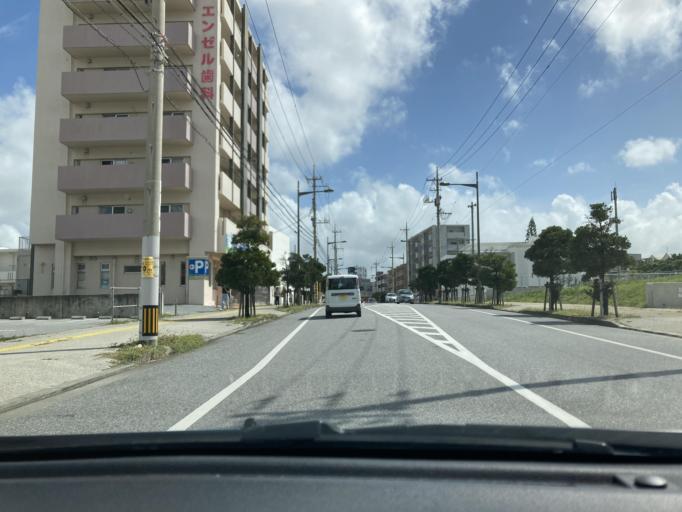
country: JP
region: Okinawa
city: Ginowan
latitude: 26.2720
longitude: 127.7308
